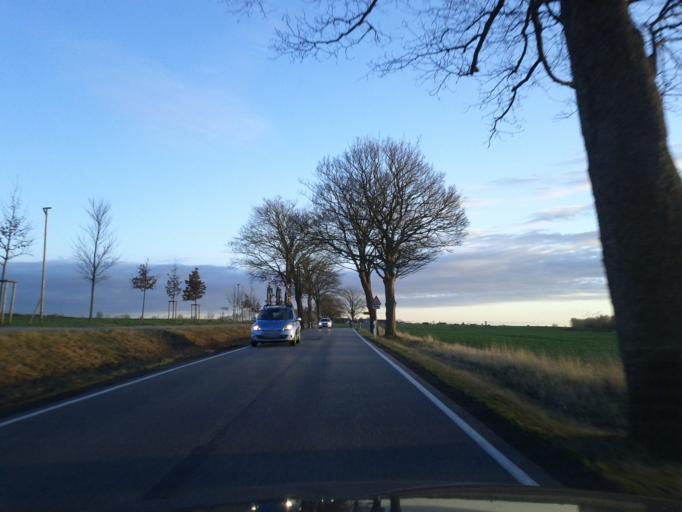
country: DE
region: Mecklenburg-Vorpommern
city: Hornstorf
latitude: 53.9462
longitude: 11.4864
